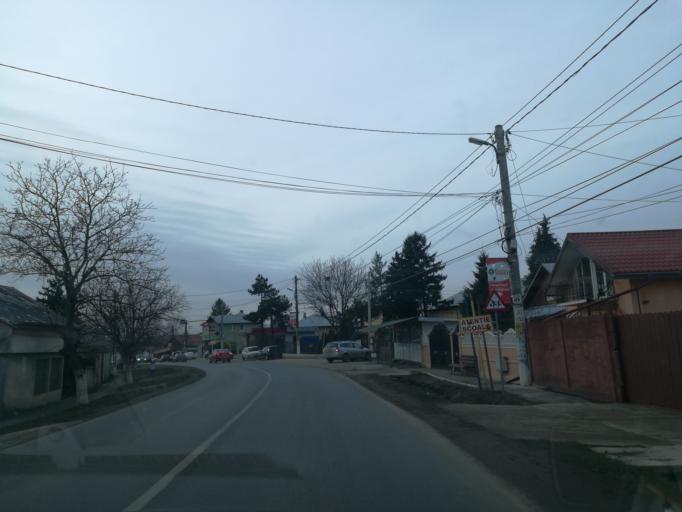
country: RO
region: Ilfov
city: Stefanestii de Jos
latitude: 44.5384
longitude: 26.2022
